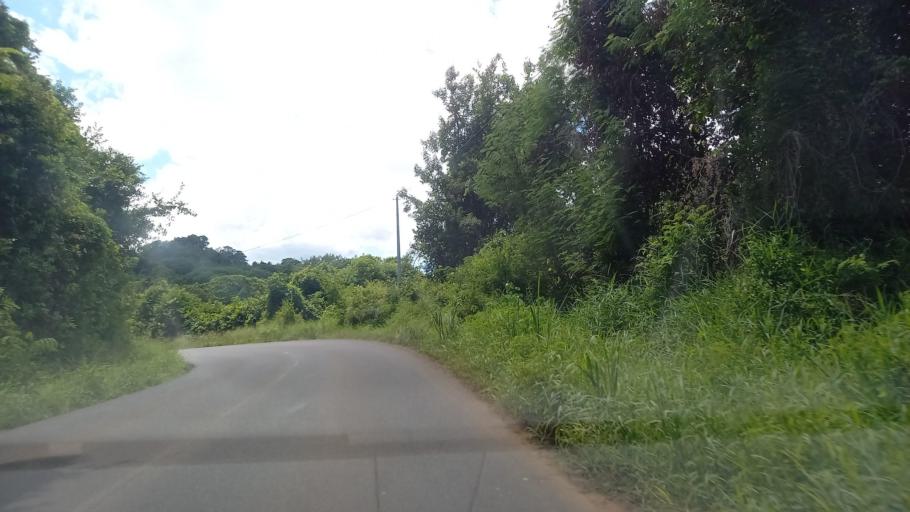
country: YT
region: Ouangani
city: Ouangani
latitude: -12.8837
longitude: 45.1298
